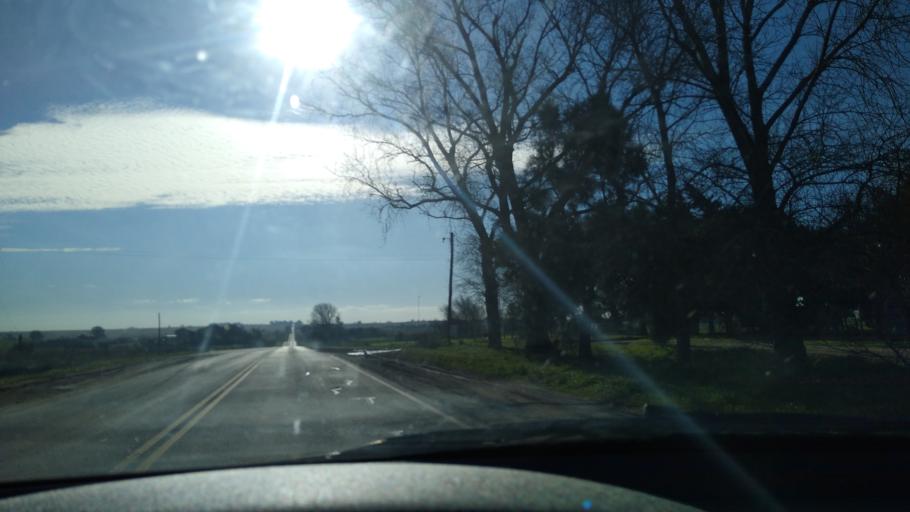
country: AR
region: Entre Rios
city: Aranguren
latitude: -32.3634
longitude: -60.3469
